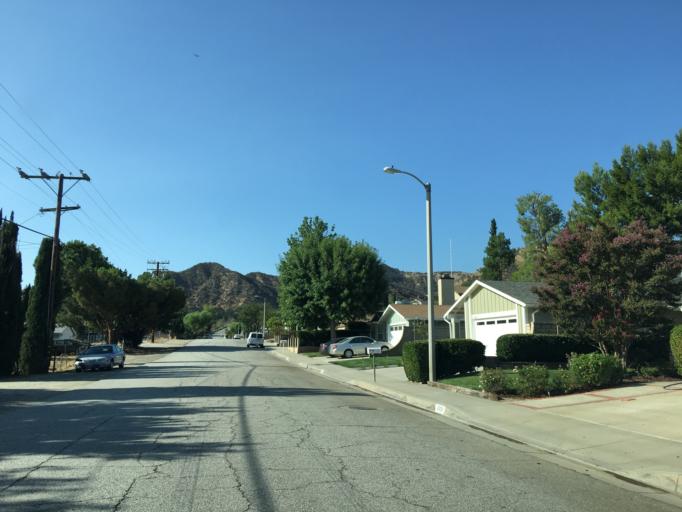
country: US
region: California
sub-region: Los Angeles County
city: Castaic
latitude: 34.4921
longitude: -118.6257
